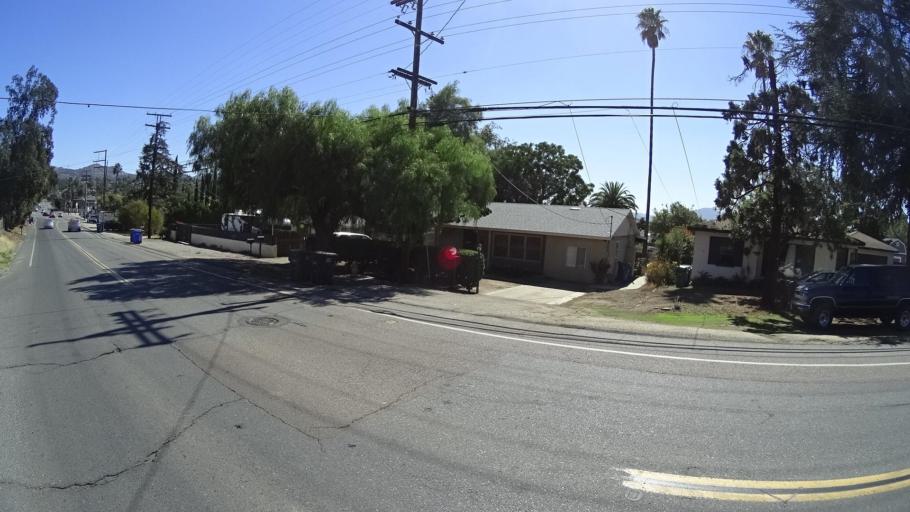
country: US
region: California
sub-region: San Diego County
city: Winter Gardens
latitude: 32.8208
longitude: -116.9367
